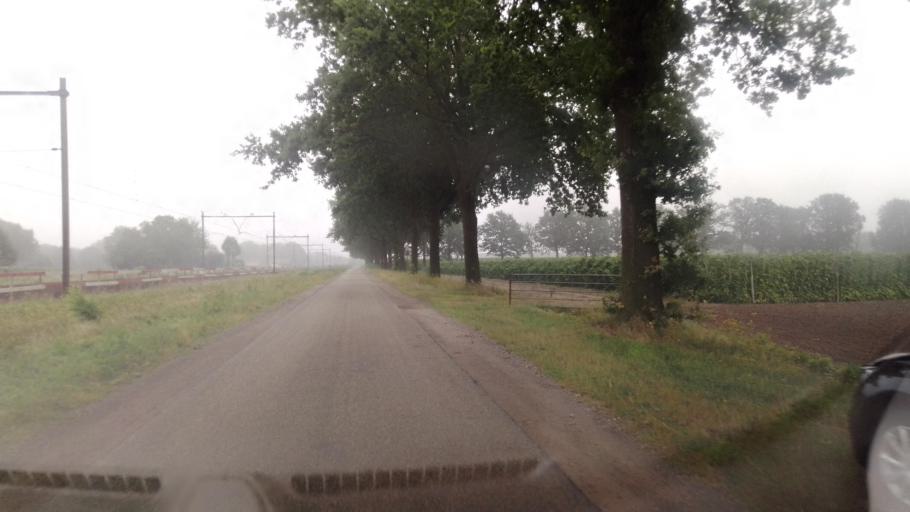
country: NL
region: Limburg
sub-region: Gemeente Peel en Maas
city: Maasbree
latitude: 51.4313
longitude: 6.0212
